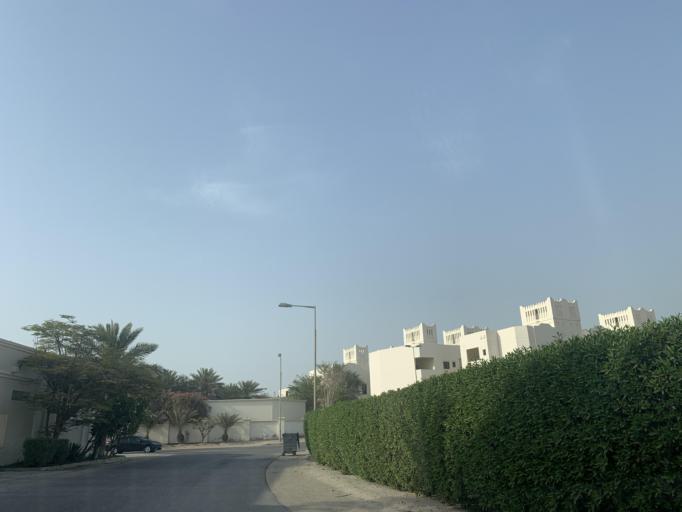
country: BH
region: Central Governorate
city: Madinat Hamad
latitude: 26.1782
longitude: 50.4761
